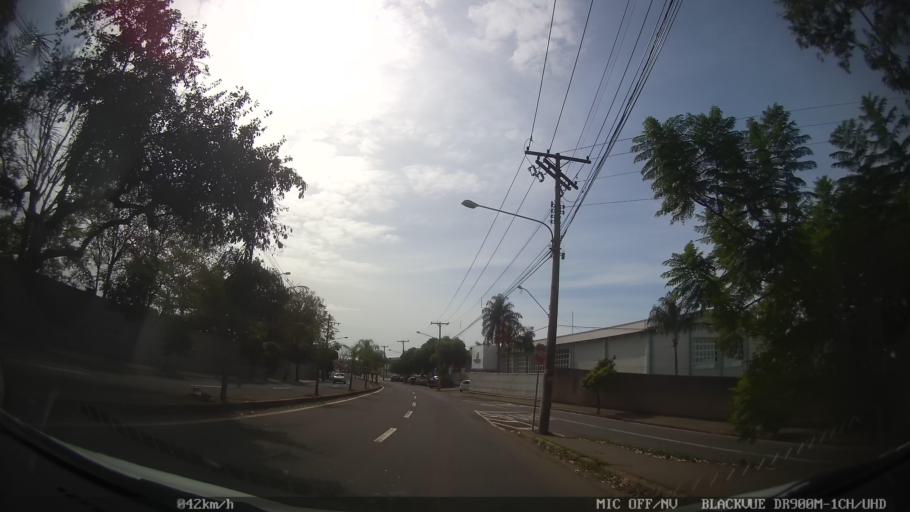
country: BR
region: Sao Paulo
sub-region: Piracicaba
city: Piracicaba
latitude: -22.7550
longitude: -47.6371
